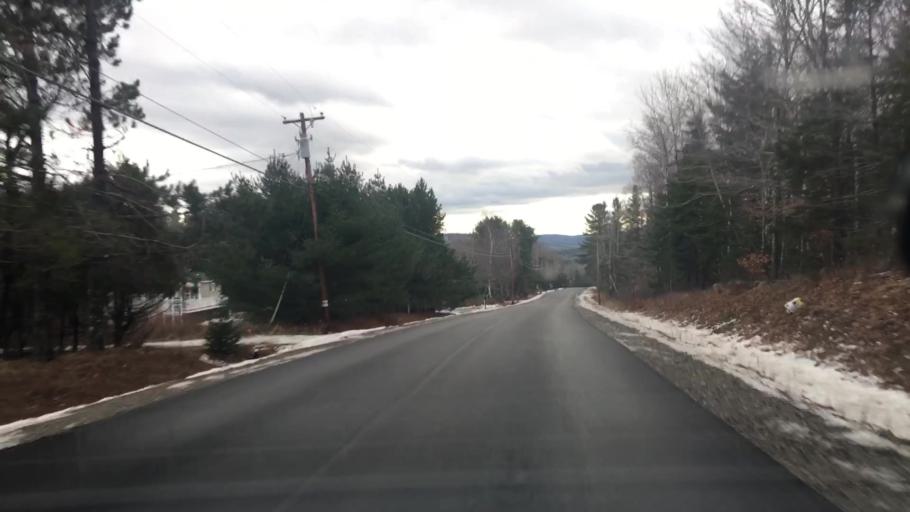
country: US
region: Maine
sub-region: Hancock County
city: Dedham
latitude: 44.6574
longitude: -68.7044
